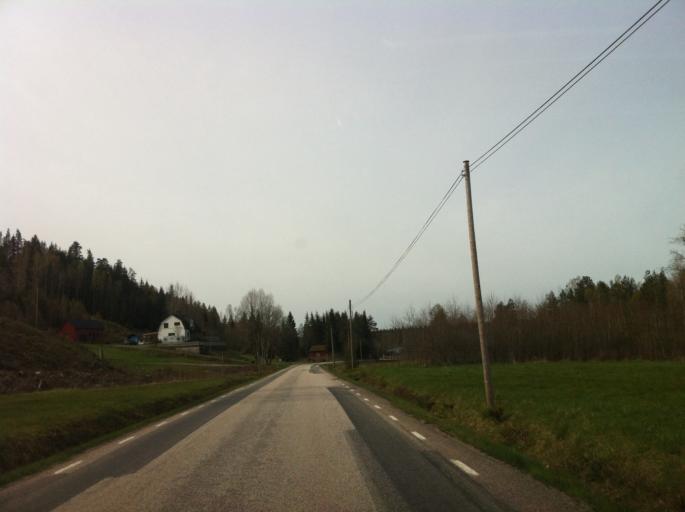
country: SE
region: Vaestra Goetaland
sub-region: Bollebygds Kommun
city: Bollebygd
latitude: 57.7450
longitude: 12.6046
